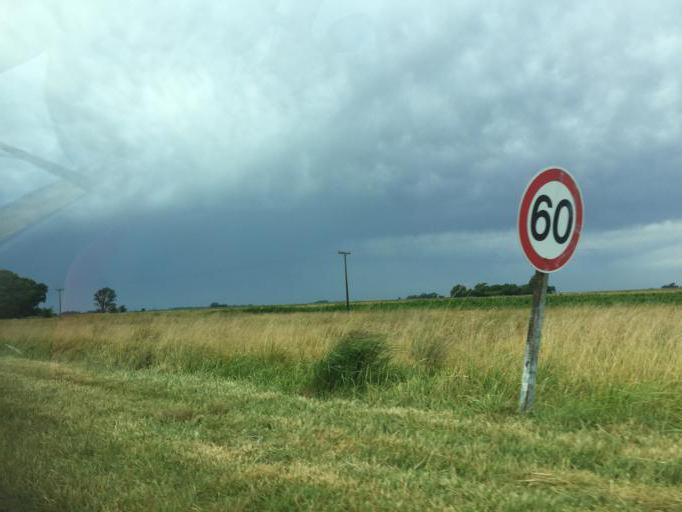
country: AR
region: Buenos Aires
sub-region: Partido de Rauch
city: Rauch
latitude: -36.9801
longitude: -58.9980
